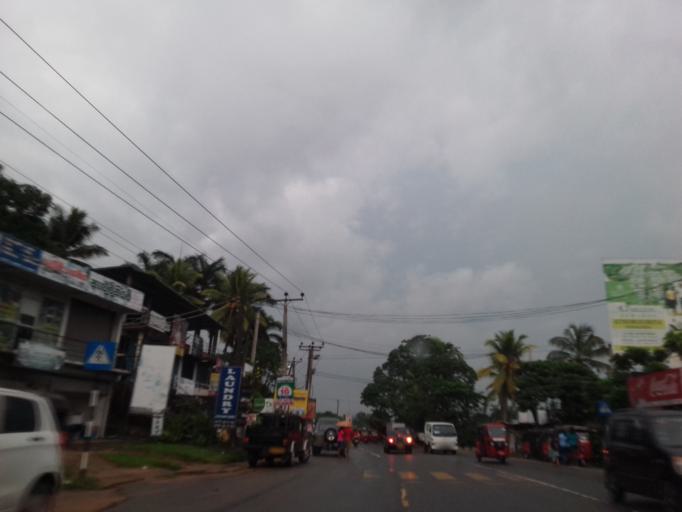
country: LK
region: Western
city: Homagama
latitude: 6.8836
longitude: 79.9706
